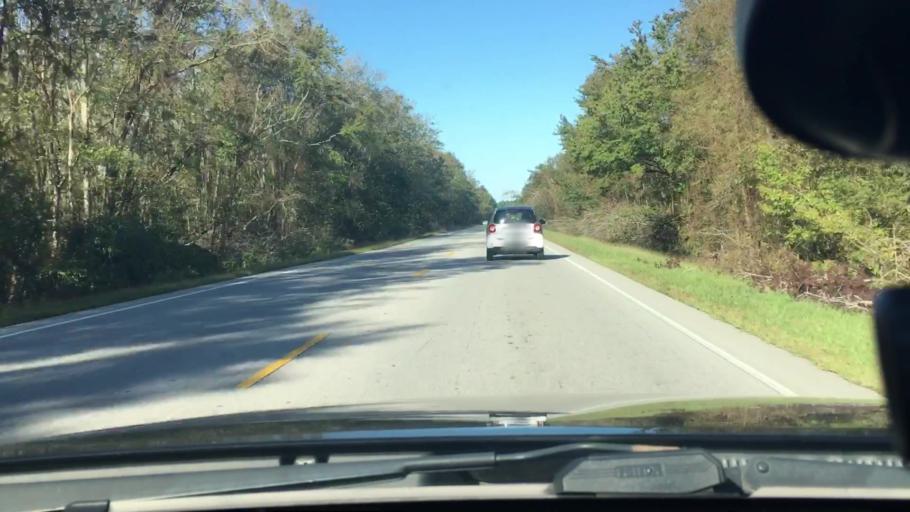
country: US
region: North Carolina
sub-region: Craven County
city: Vanceboro
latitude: 35.2045
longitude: -77.1270
